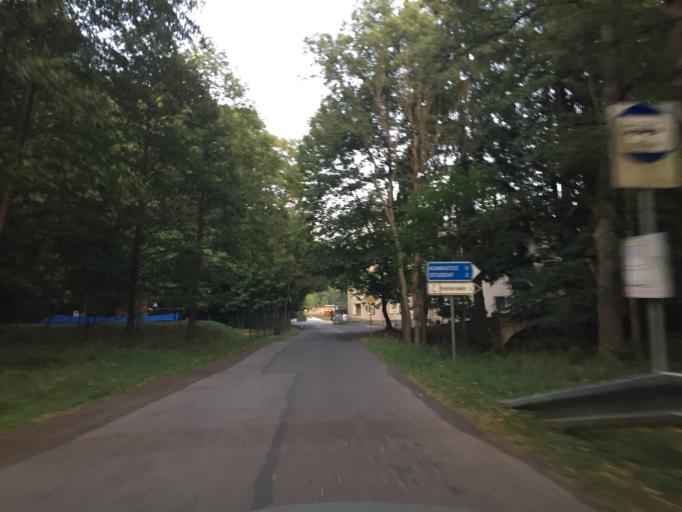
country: CZ
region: Ustecky
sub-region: Okres Decin
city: Chribska
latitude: 50.8591
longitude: 14.4395
